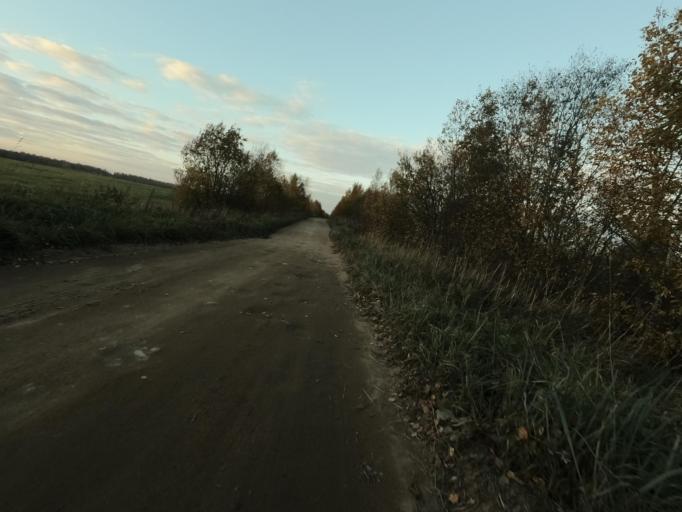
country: RU
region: Leningrad
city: Mga
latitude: 59.7991
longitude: 31.2002
